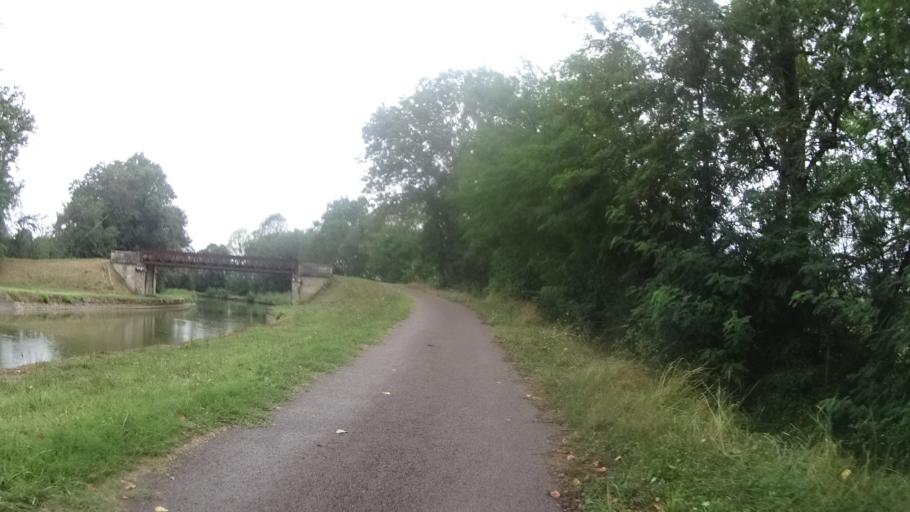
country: FR
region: Bourgogne
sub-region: Departement de la Nievre
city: Saint-Leger-des-Vignes
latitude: 46.8194
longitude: 3.4250
